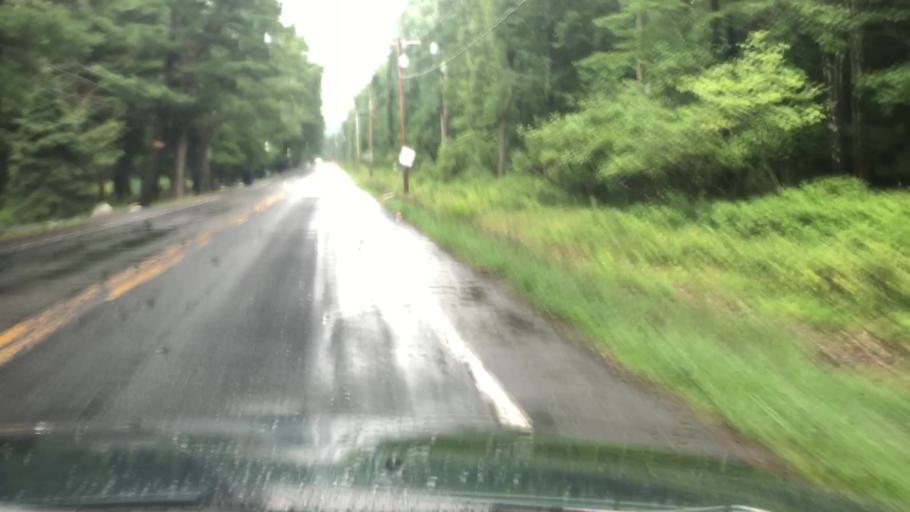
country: US
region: Pennsylvania
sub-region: Monroe County
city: Mountainhome
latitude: 41.2293
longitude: -75.2324
